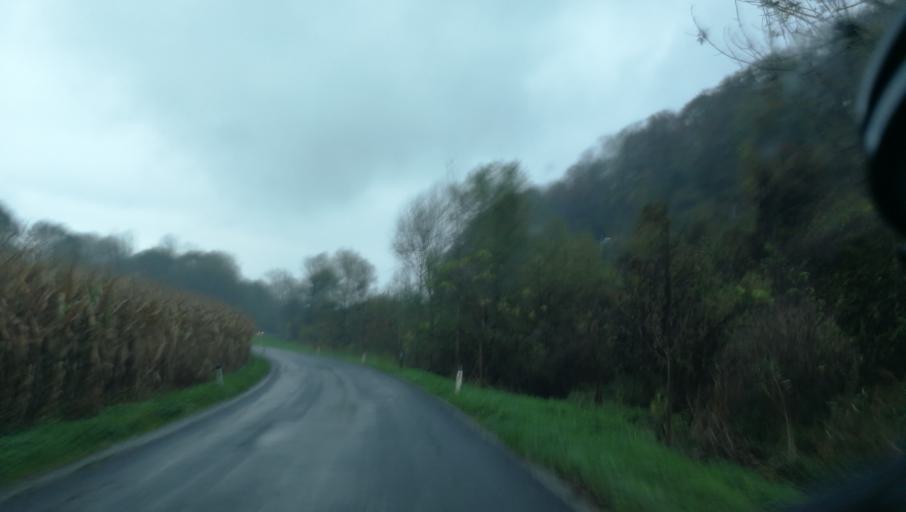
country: AT
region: Styria
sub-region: Politischer Bezirk Leibnitz
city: Strass in Steiermark
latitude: 46.7148
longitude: 15.6200
